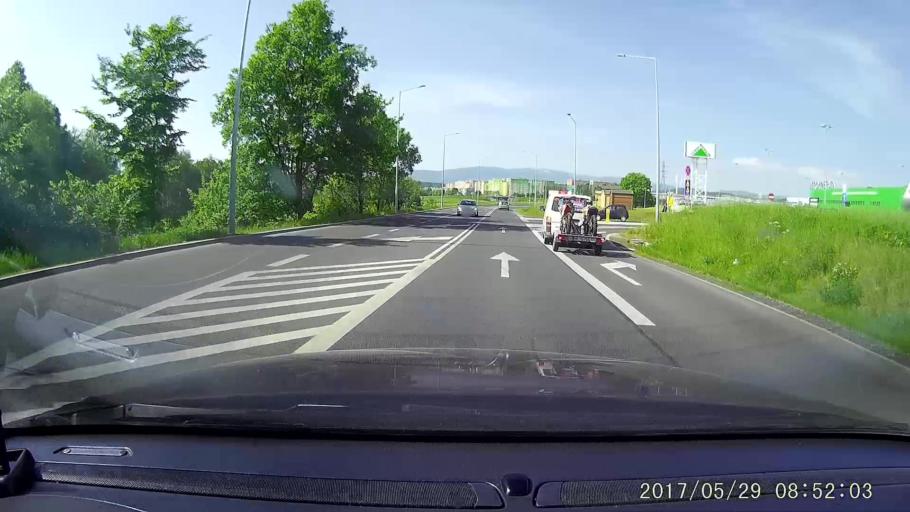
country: PL
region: Lower Silesian Voivodeship
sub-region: Powiat jeleniogorski
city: Jezow Sudecki
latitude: 50.9239
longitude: 15.7688
